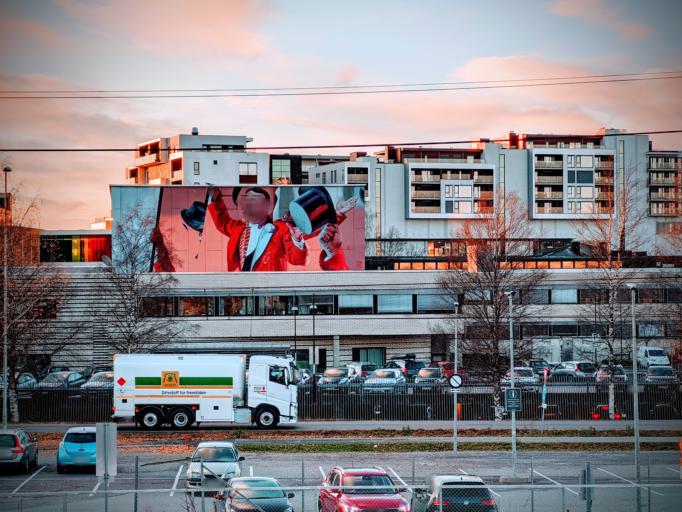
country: NO
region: Akershus
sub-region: Ullensaker
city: Jessheim
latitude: 60.1432
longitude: 11.1782
